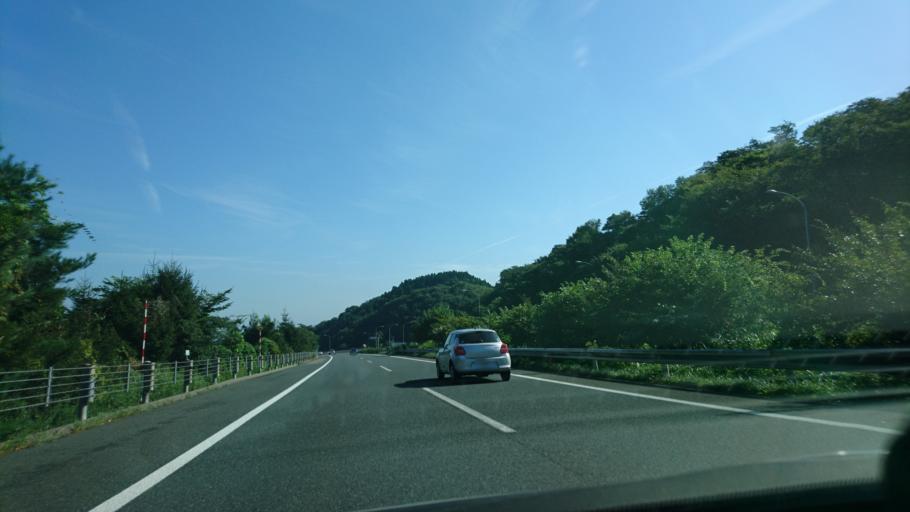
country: JP
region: Iwate
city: Ichinoseki
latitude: 38.9613
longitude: 141.1101
